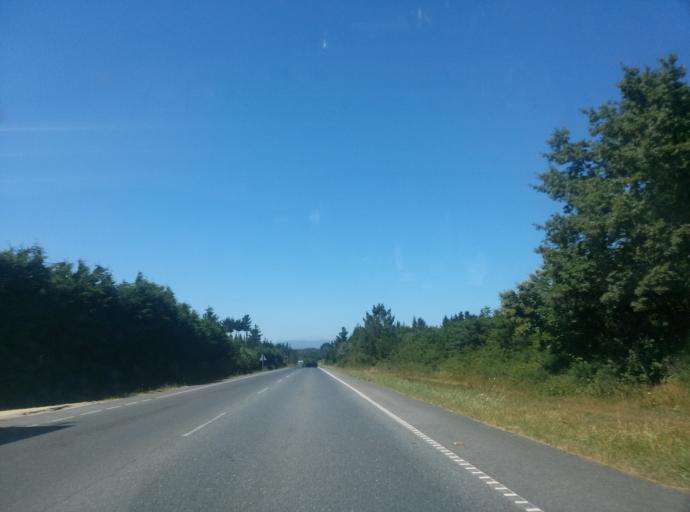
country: ES
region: Galicia
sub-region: Provincia de Lugo
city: Mos
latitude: 43.1123
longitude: -7.4840
